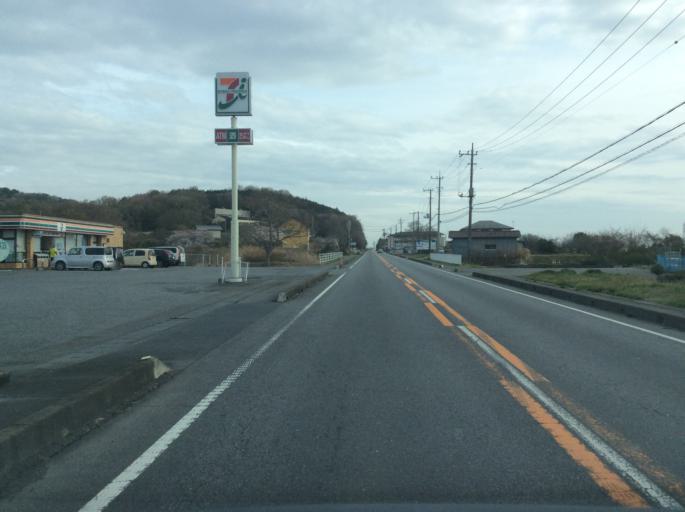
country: JP
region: Ibaraki
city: Tsukuba
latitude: 36.1666
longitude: 140.1067
